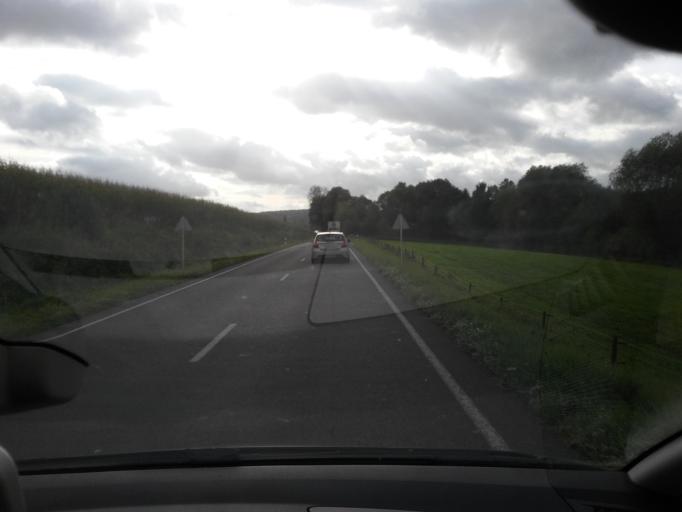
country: LU
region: Diekirch
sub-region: Canton de Redange
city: Ell
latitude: 49.7323
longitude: 5.8501
